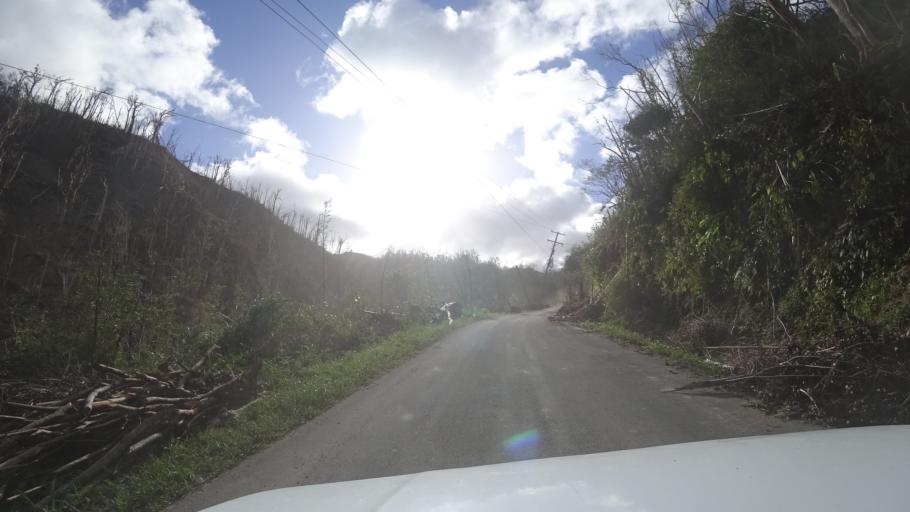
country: DM
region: Saint Patrick
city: Berekua
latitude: 15.2645
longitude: -61.3319
